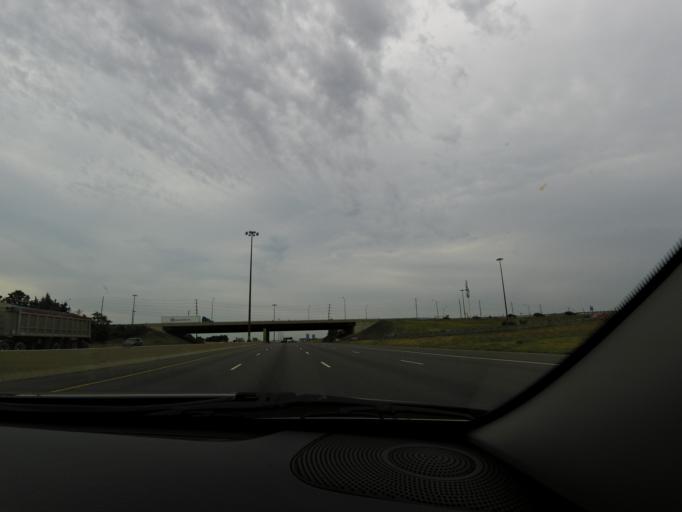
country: CA
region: Ontario
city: Vaughan
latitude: 43.8299
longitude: -79.5466
